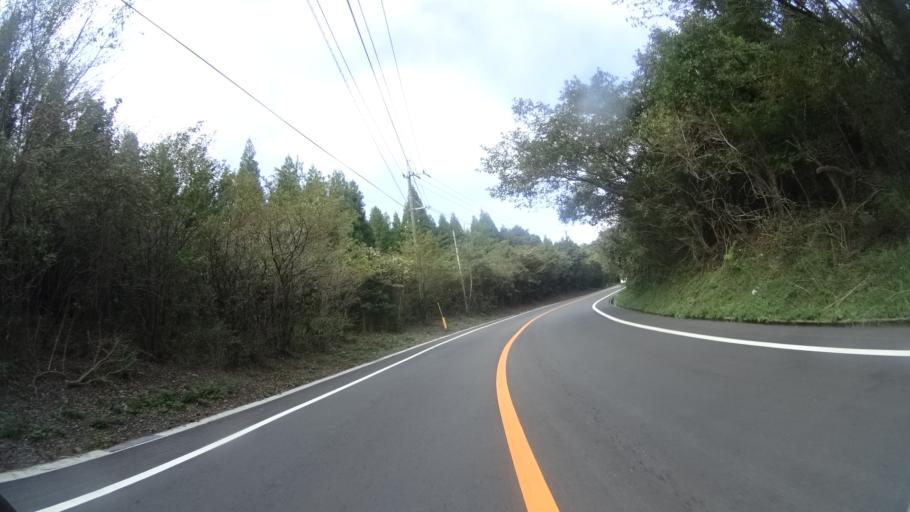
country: JP
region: Kumamoto
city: Aso
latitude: 32.9492
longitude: 130.9787
